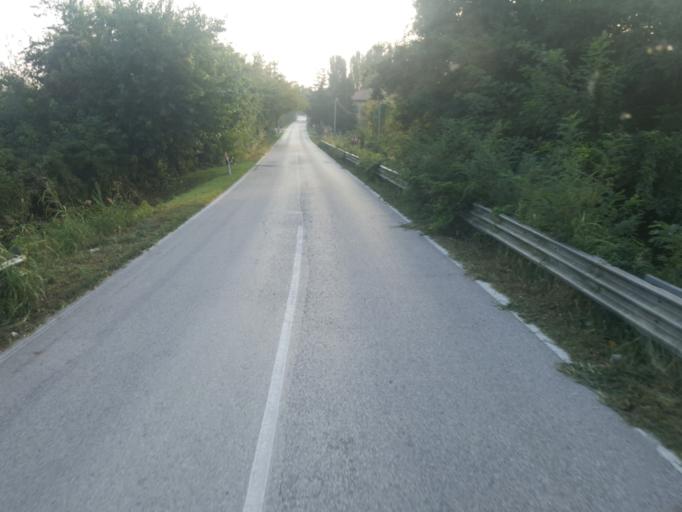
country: IT
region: Emilia-Romagna
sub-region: Provincia di Ferrara
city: San Biagio
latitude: 44.5781
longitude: 11.8765
